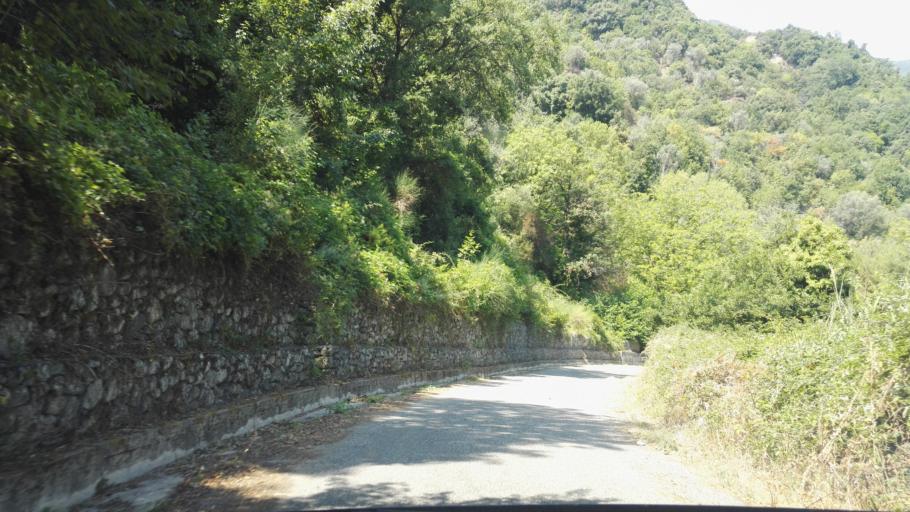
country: IT
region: Calabria
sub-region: Provincia di Reggio Calabria
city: Bivongi
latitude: 38.4901
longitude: 16.4175
